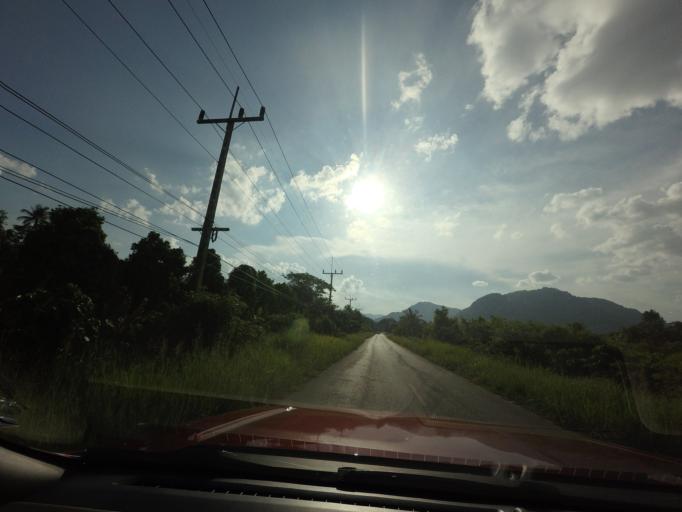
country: TH
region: Yala
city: Ban Nang Sata
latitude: 6.2224
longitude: 101.2275
